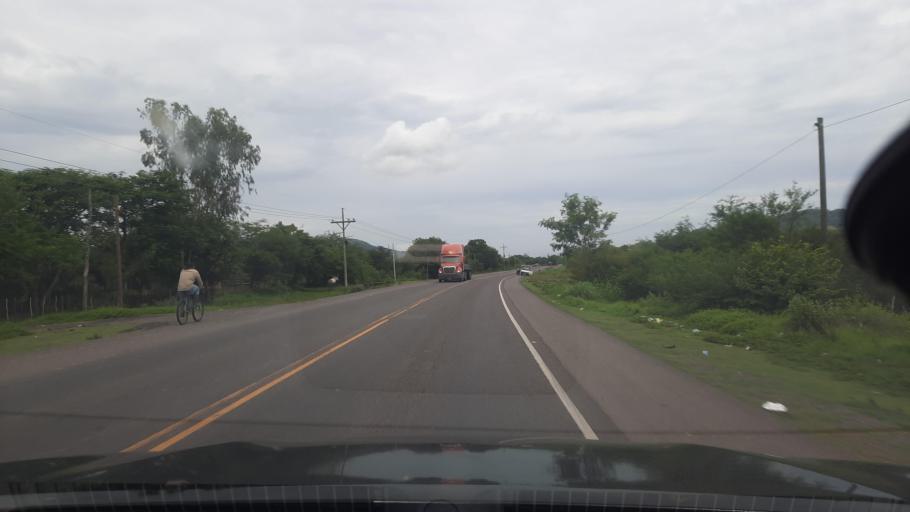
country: HN
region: Valle
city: Jicaro Galan
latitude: 13.5239
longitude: -87.4386
